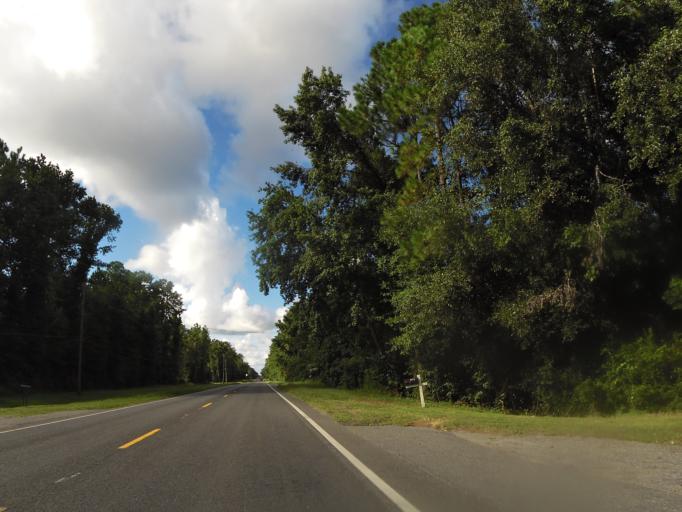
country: US
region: Georgia
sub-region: Camden County
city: Woodbine
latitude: 30.9168
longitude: -81.7132
